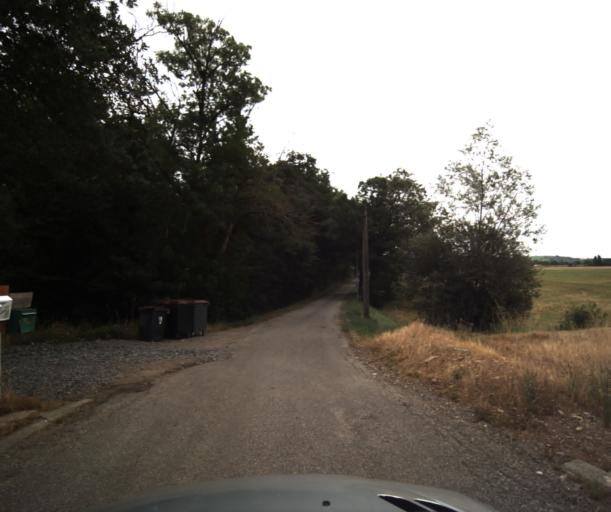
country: FR
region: Midi-Pyrenees
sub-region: Departement de la Haute-Garonne
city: Labarthe-sur-Leze
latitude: 43.4667
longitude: 1.4061
